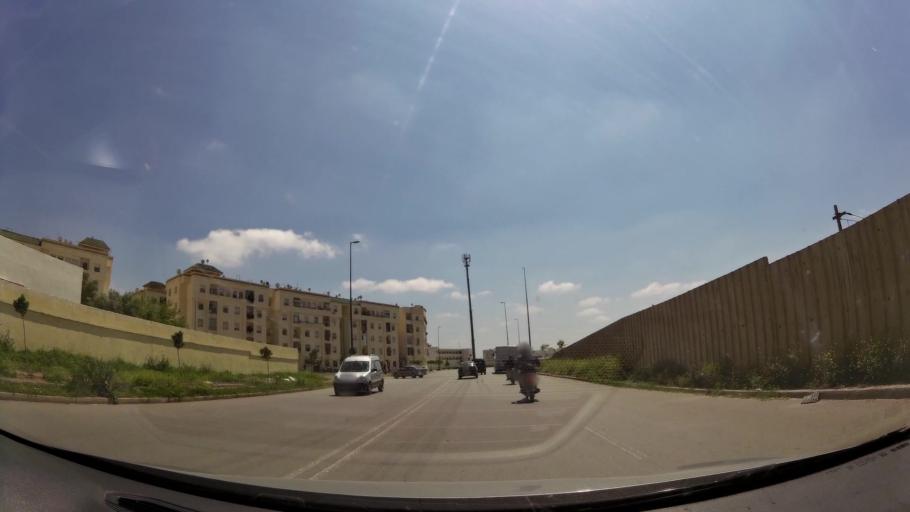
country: MA
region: Fes-Boulemane
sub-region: Fes
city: Fes
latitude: 34.0162
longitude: -5.0437
